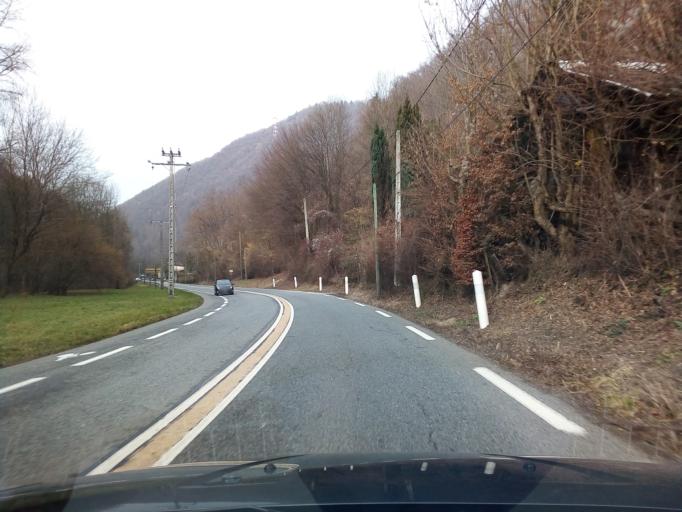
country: FR
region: Rhone-Alpes
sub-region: Departement de l'Isere
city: Herbeys
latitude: 45.1616
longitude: 5.8167
